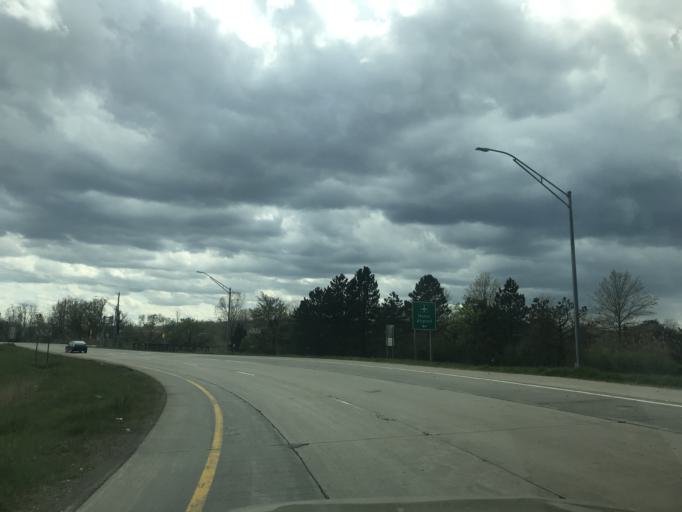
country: US
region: Michigan
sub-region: Wayne County
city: Romulus
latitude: 42.1957
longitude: -83.3915
